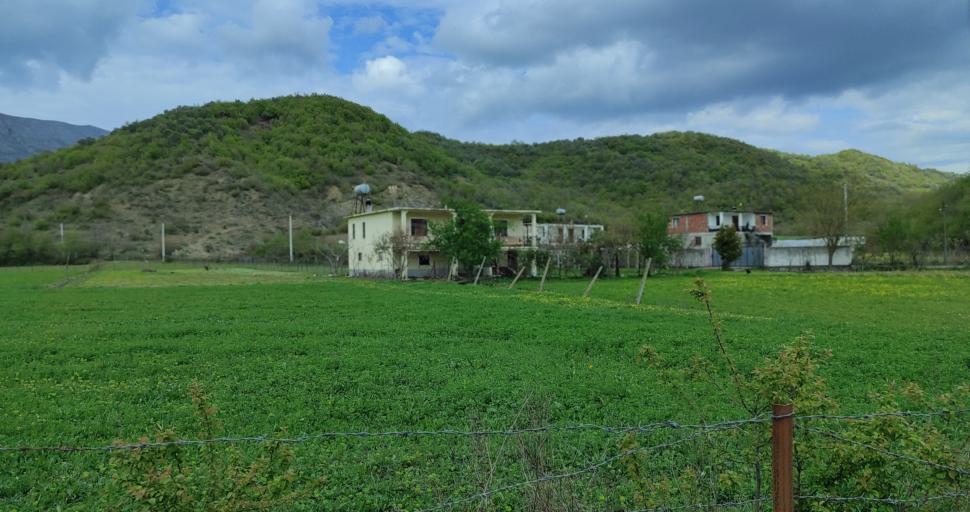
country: AL
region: Shkoder
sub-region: Rrethi i Shkodres
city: Dajc
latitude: 42.0269
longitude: 19.4198
